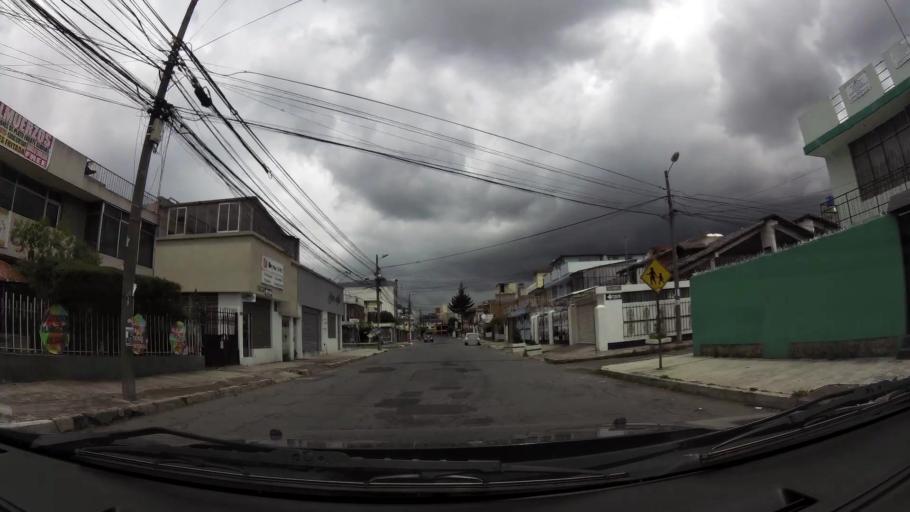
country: EC
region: Pichincha
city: Quito
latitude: -0.1663
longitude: -78.4783
